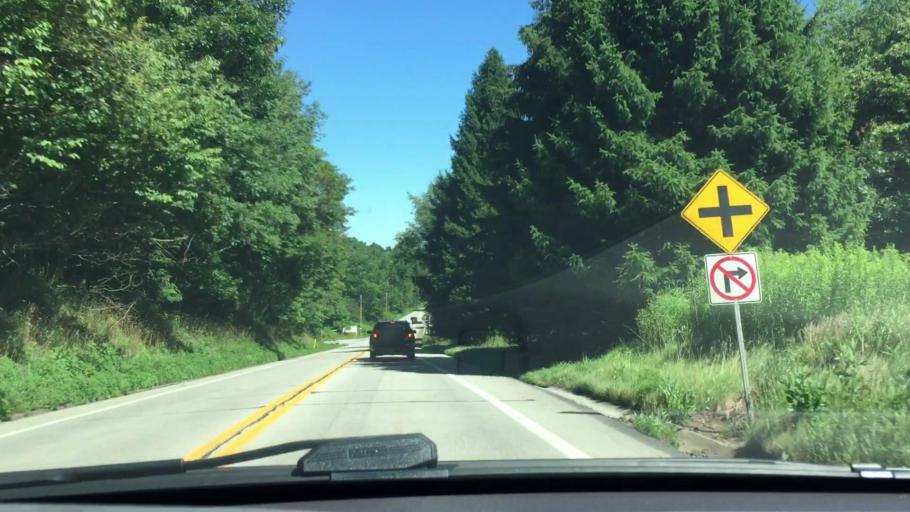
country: US
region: Pennsylvania
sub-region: Westmoreland County
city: West Leechburg
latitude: 40.6231
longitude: -79.6402
